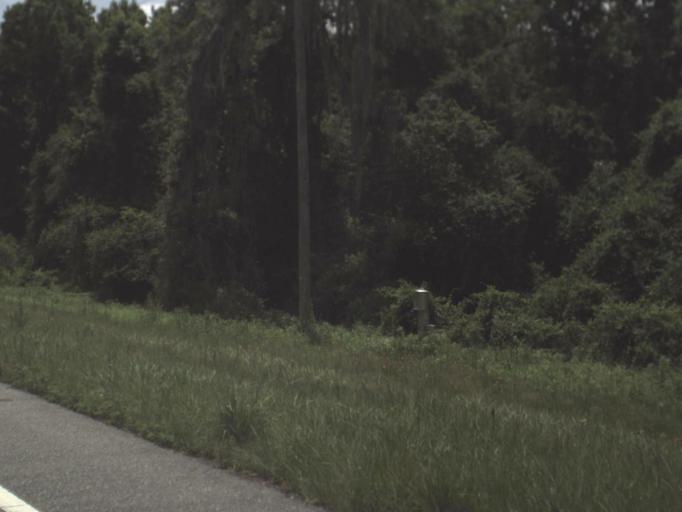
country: US
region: Florida
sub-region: Madison County
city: Madison
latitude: 30.4888
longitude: -83.4708
